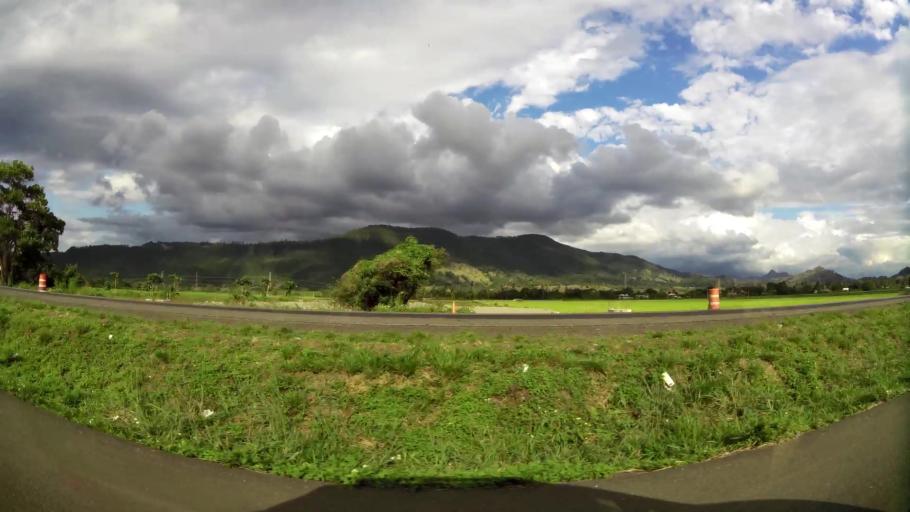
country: DO
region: Monsenor Nouel
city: Bonao
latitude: 18.8943
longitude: -70.3686
